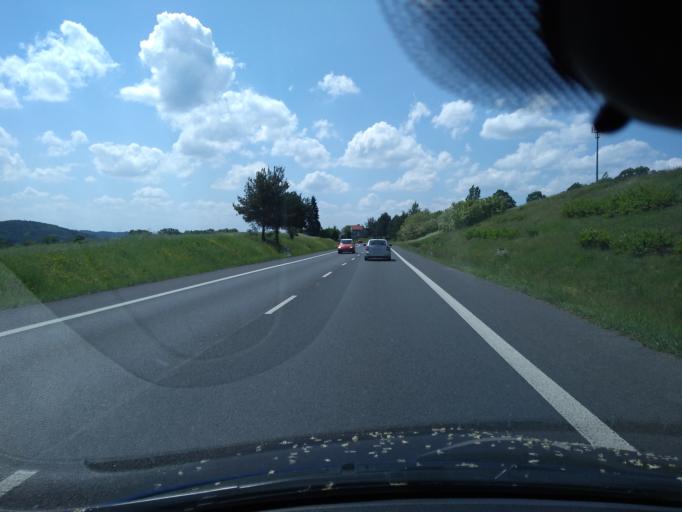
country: CZ
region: Plzensky
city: Svihov
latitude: 49.5057
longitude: 13.2966
